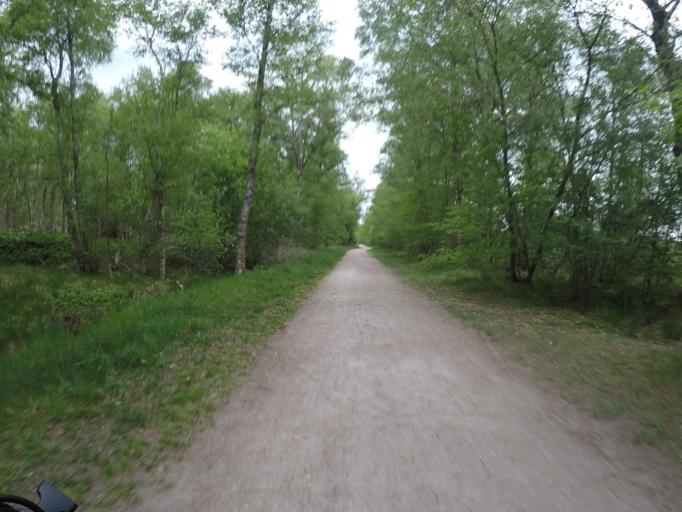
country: DE
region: Schleswig-Holstein
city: Henstedt-Ulzburg
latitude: 53.7532
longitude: 10.0123
